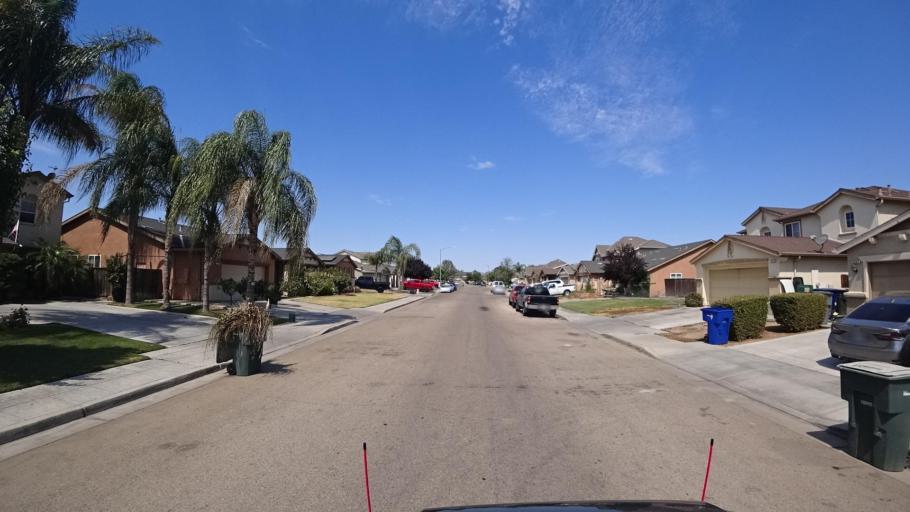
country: US
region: California
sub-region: Fresno County
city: Sunnyside
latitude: 36.7191
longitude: -119.7149
